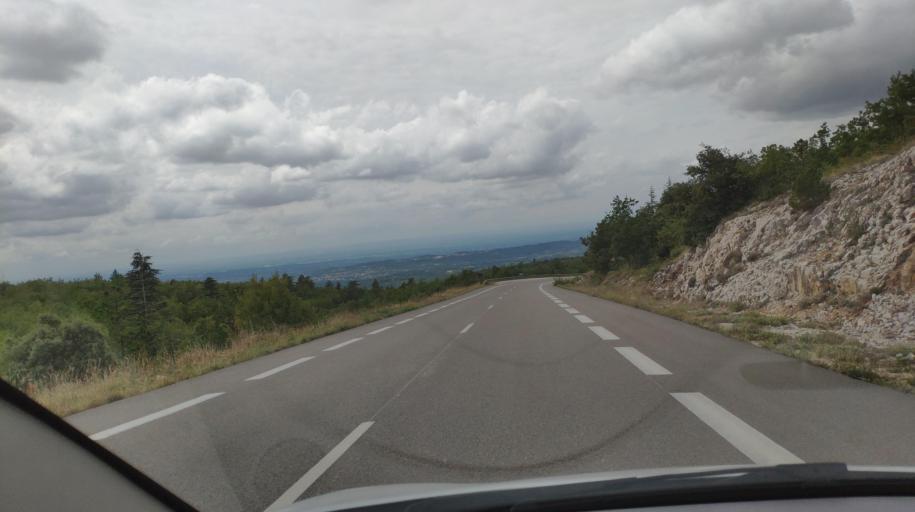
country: FR
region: Provence-Alpes-Cote d'Azur
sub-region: Departement du Vaucluse
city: Villes-sur-Auzon
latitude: 44.0831
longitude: 5.2803
